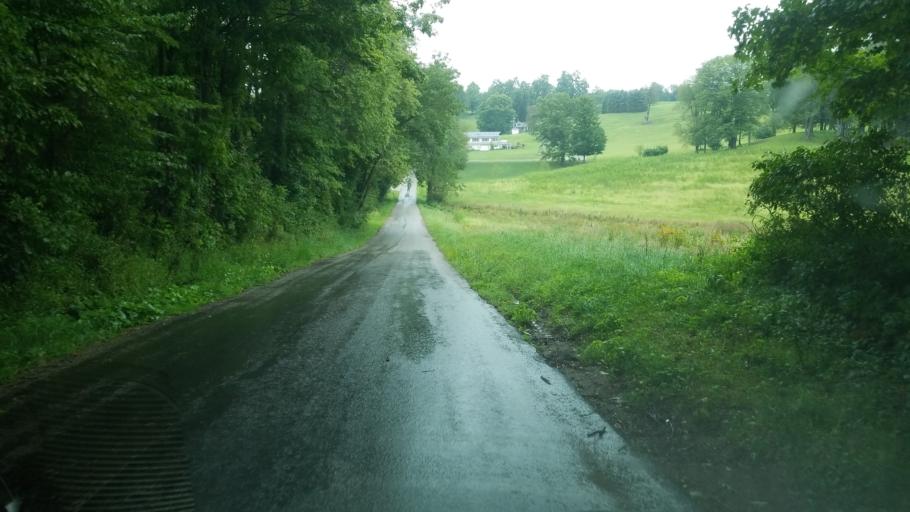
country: US
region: Ohio
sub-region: Sandusky County
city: Bellville
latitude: 40.6315
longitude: -82.4910
